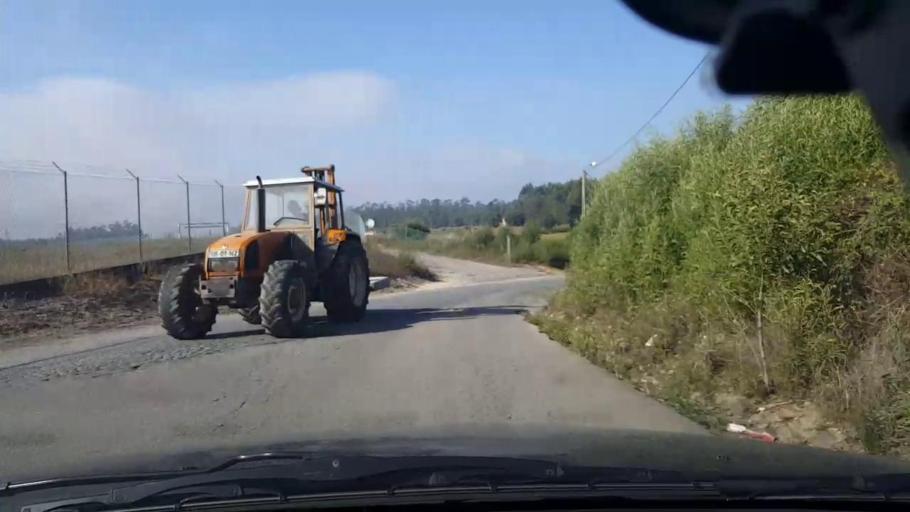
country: PT
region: Porto
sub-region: Matosinhos
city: Lavra
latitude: 41.2650
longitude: -8.6834
